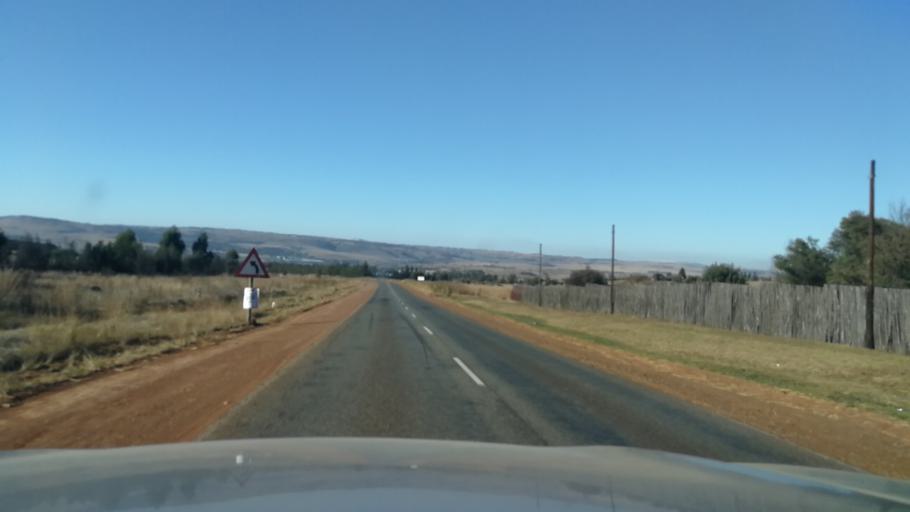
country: ZA
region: Gauteng
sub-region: West Rand District Municipality
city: Krugersdorp
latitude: -25.9983
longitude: 27.7009
